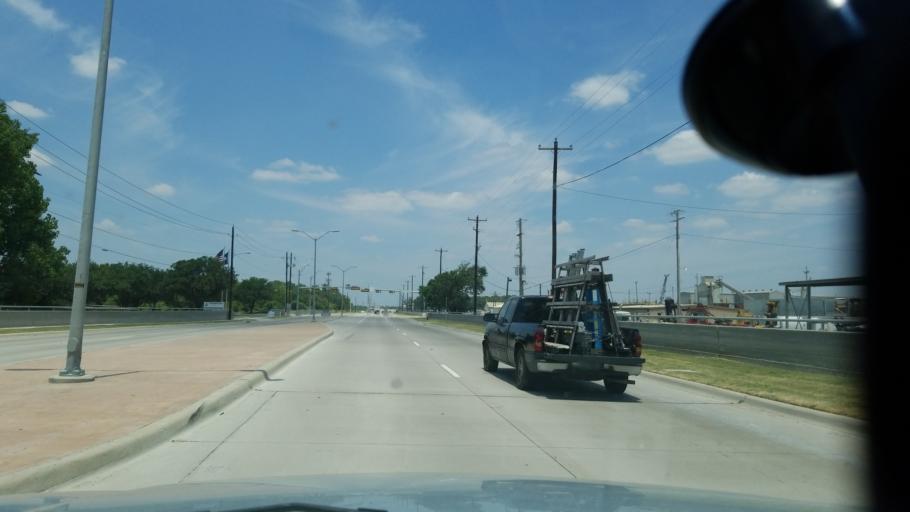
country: US
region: Texas
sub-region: Dallas County
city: Grand Prairie
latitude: 32.7649
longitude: -96.9602
